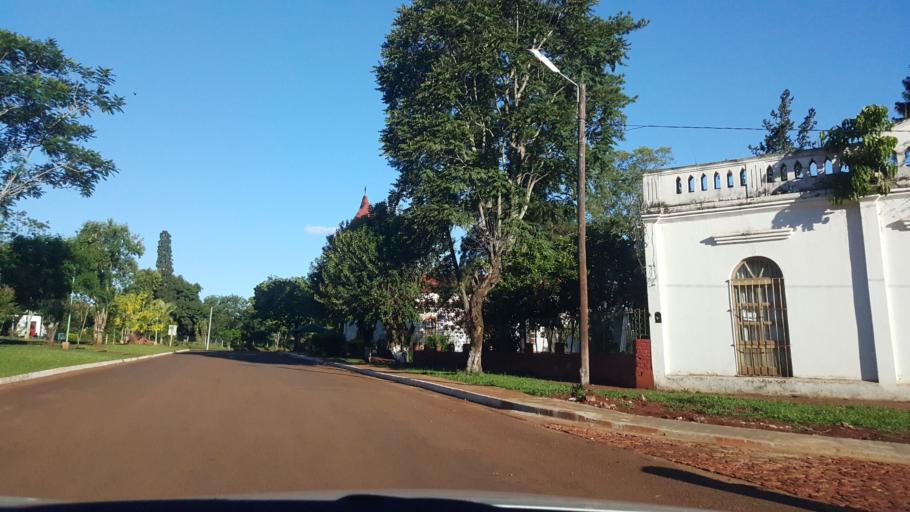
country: AR
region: Misiones
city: Gobernador Roca
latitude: -27.1300
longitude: -55.5114
